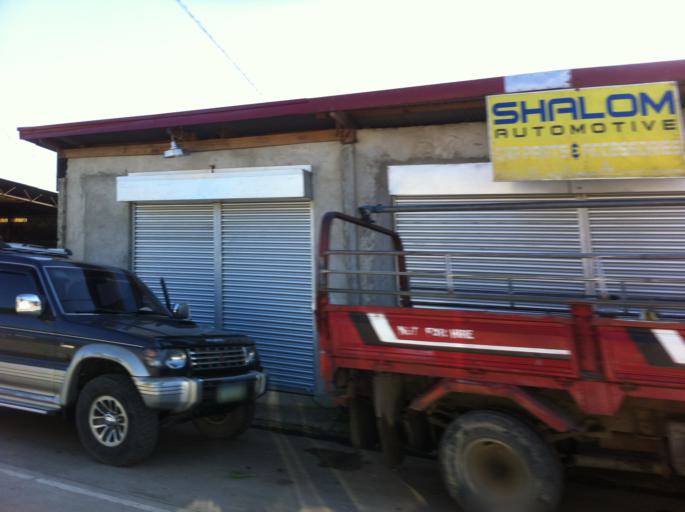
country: PH
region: Cordillera
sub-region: Province of Benguet
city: La Trinidad
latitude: 16.4471
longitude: 120.5769
